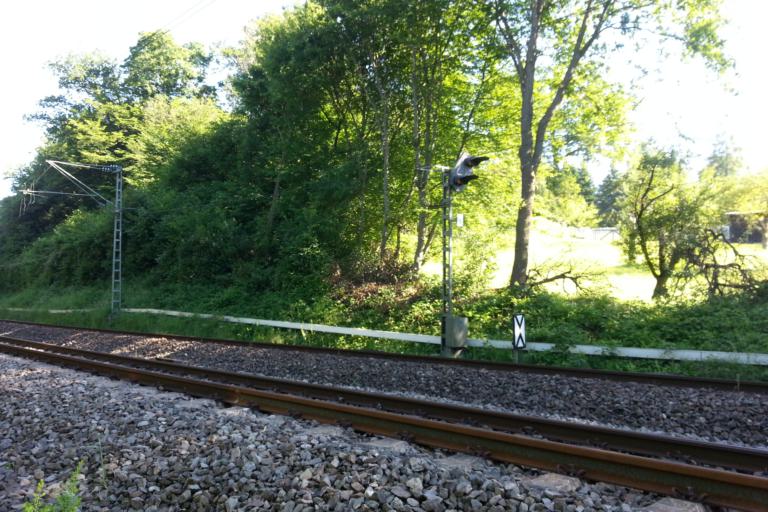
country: DE
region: Baden-Wuerttemberg
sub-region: Regierungsbezirk Stuttgart
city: Mittelschontal
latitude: 48.9276
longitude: 9.4155
